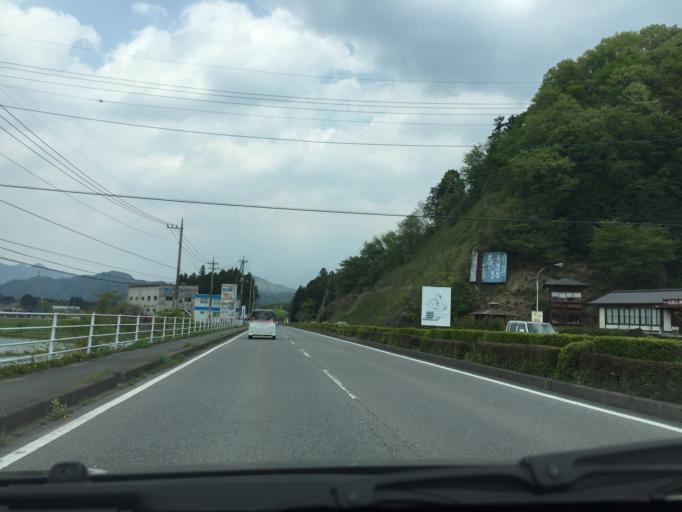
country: JP
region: Tochigi
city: Imaichi
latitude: 36.7532
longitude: 139.7152
